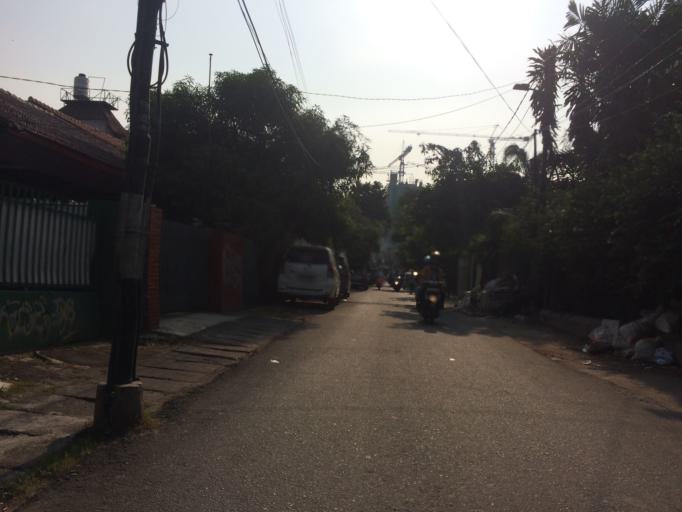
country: ID
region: Jakarta Raya
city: Jakarta
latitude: -6.2090
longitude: 106.8442
